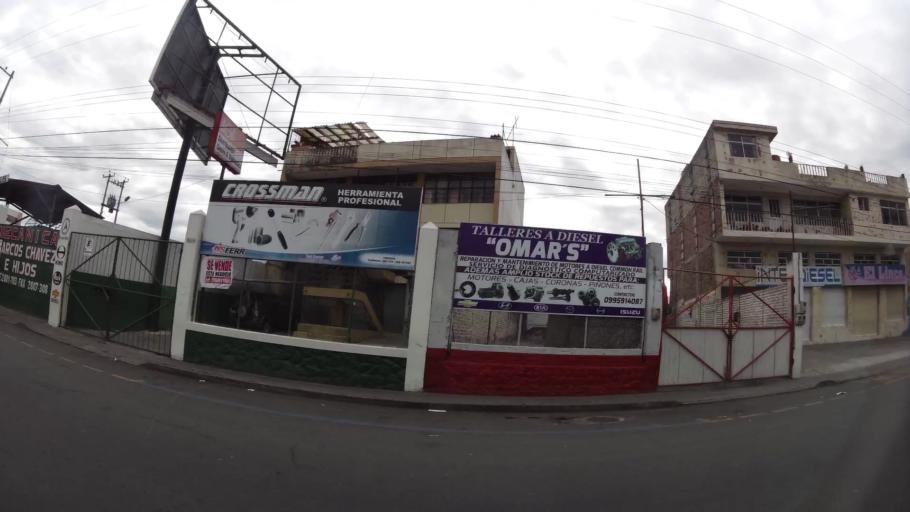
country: EC
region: Cotopaxi
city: Latacunga
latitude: -0.9282
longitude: -78.6242
